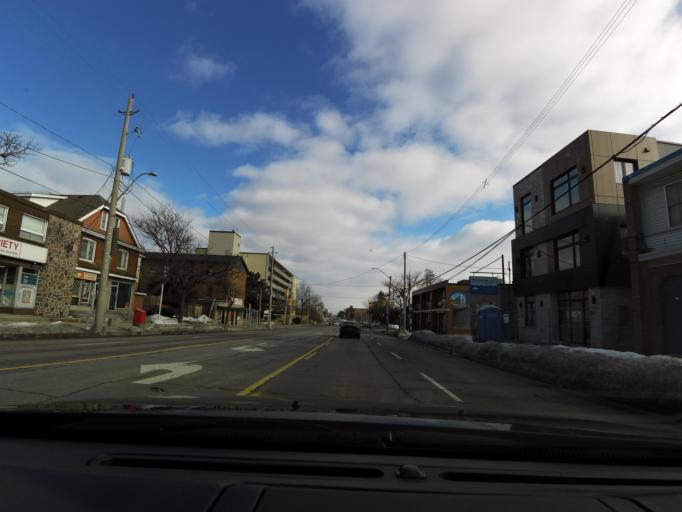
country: CA
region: Ontario
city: Hamilton
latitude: 43.2334
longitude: -79.7890
